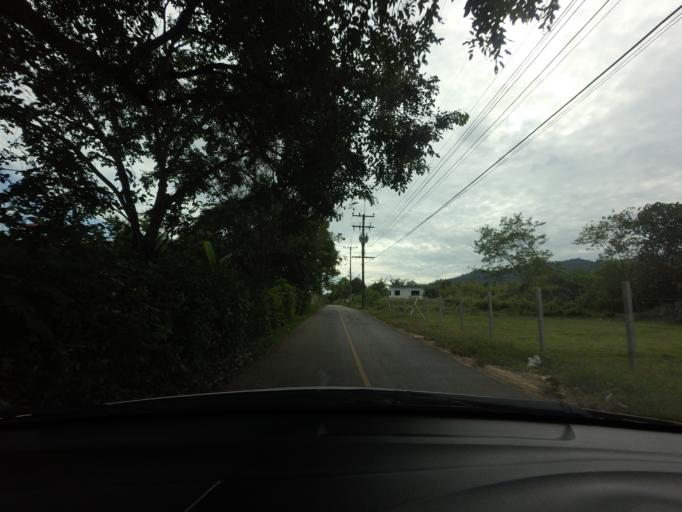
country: TH
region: Nakhon Nayok
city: Nakhon Nayok
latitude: 14.3236
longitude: 101.2893
